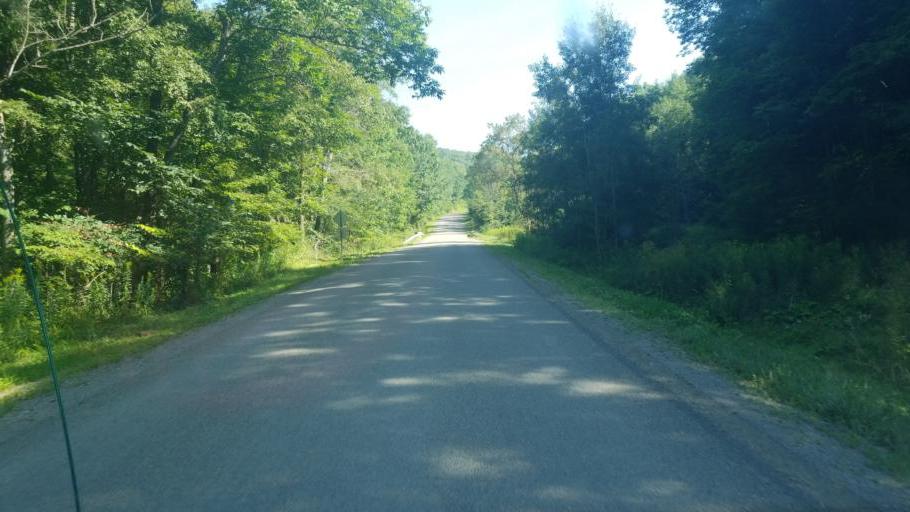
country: US
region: New York
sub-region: Allegany County
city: Wellsville
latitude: 42.0278
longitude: -77.9380
